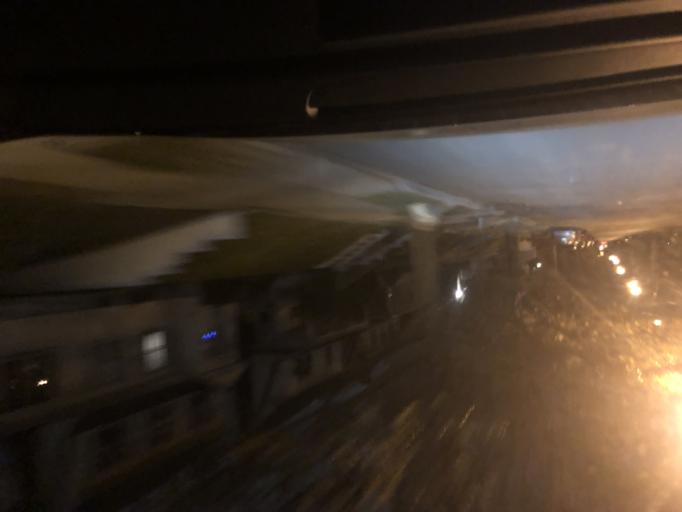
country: US
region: New Jersey
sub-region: Hudson County
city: East Newark
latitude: 40.7656
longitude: -74.1754
